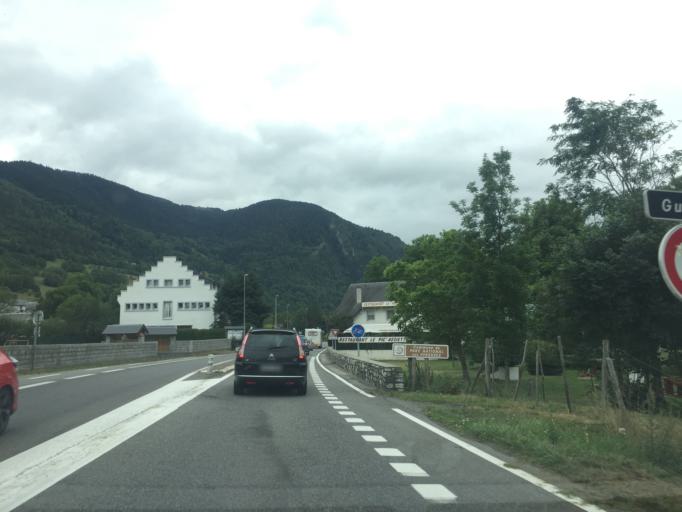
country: FR
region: Midi-Pyrenees
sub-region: Departement des Hautes-Pyrenees
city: Saint-Lary-Soulan
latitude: 42.8510
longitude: 0.3464
